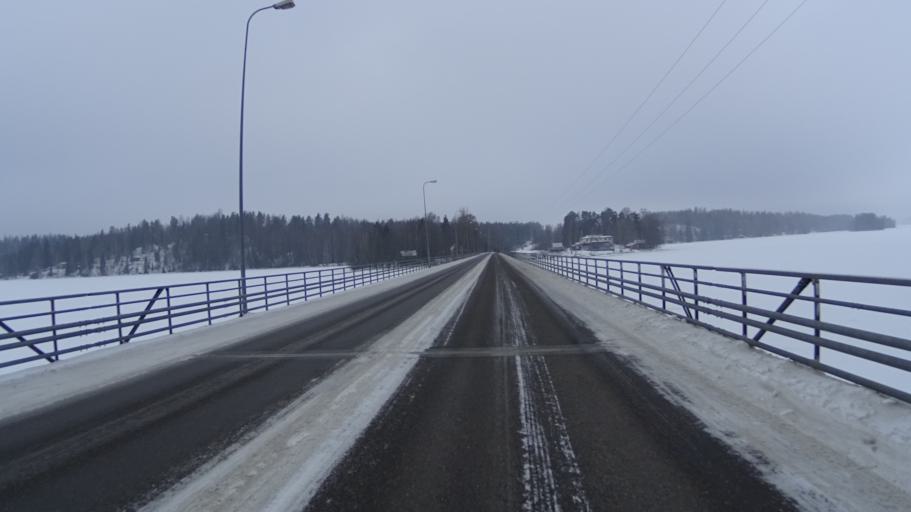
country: FI
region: Uusimaa
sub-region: Helsinki
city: Lohja
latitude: 60.3606
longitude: 24.1722
